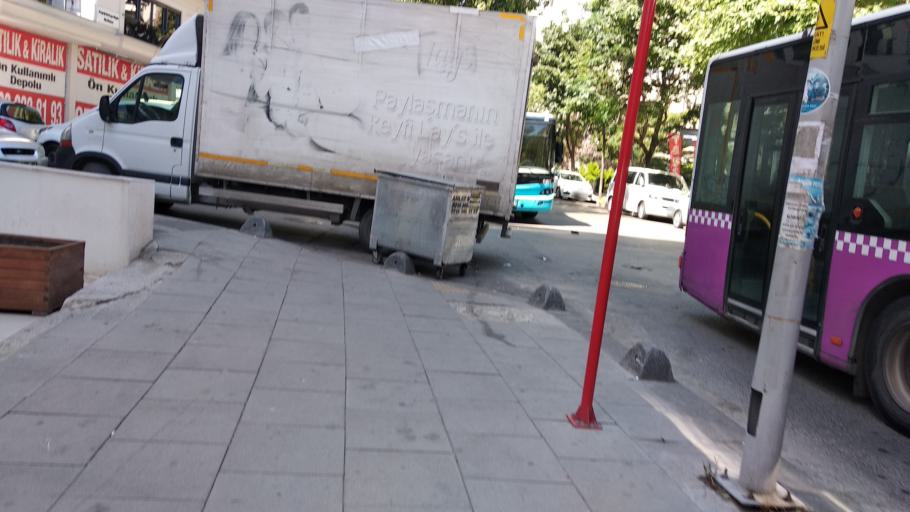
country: TR
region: Istanbul
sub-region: Atasehir
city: Atasehir
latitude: 40.9558
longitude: 29.0944
